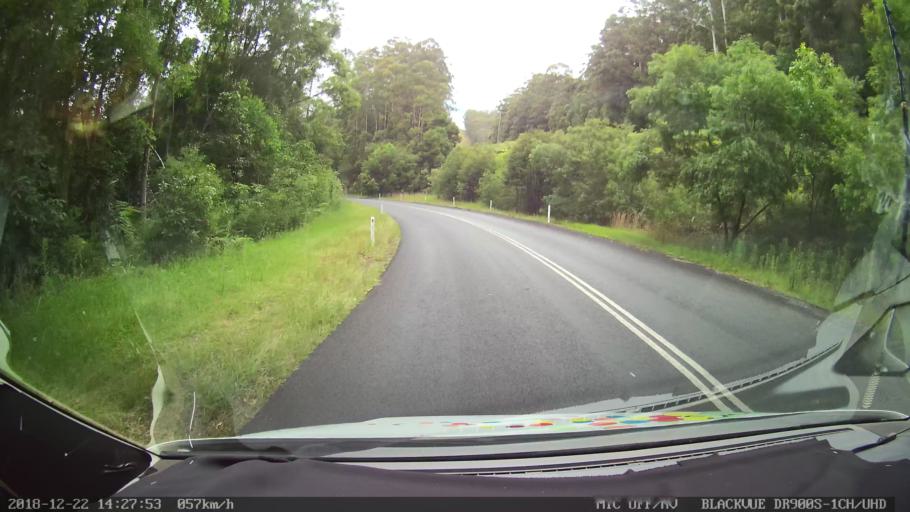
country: AU
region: New South Wales
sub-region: Bellingen
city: Dorrigo
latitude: -30.0688
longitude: 152.6357
